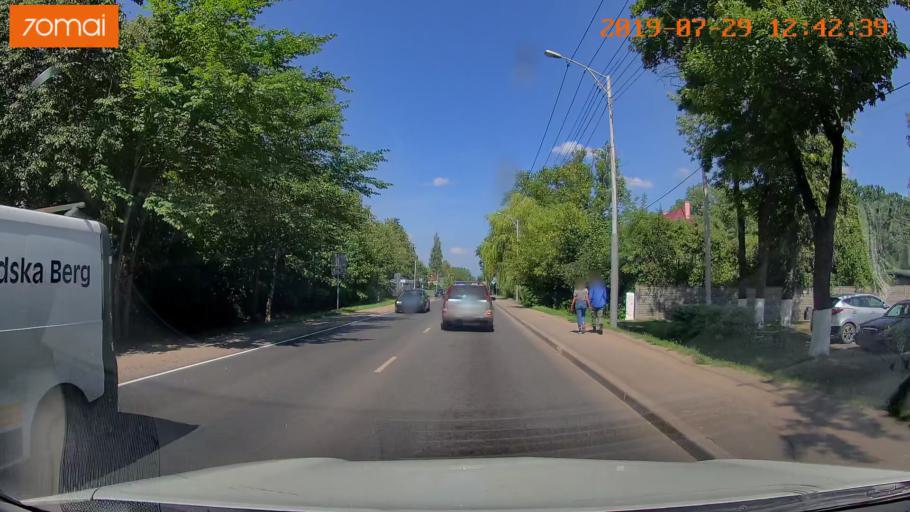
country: RU
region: Kaliningrad
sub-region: Gorod Kaliningrad
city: Kaliningrad
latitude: 54.6728
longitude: 20.5439
